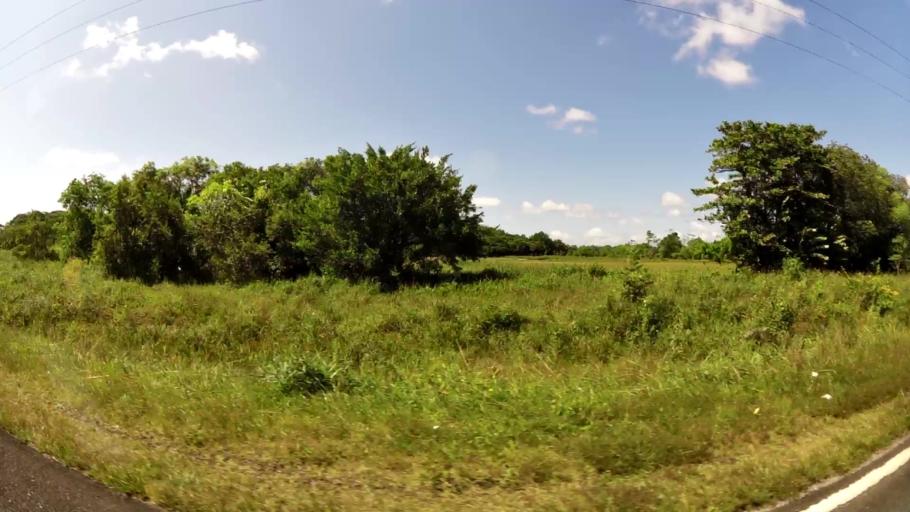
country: GF
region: Guyane
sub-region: Guyane
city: Matoury
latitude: 4.8293
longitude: -52.3540
